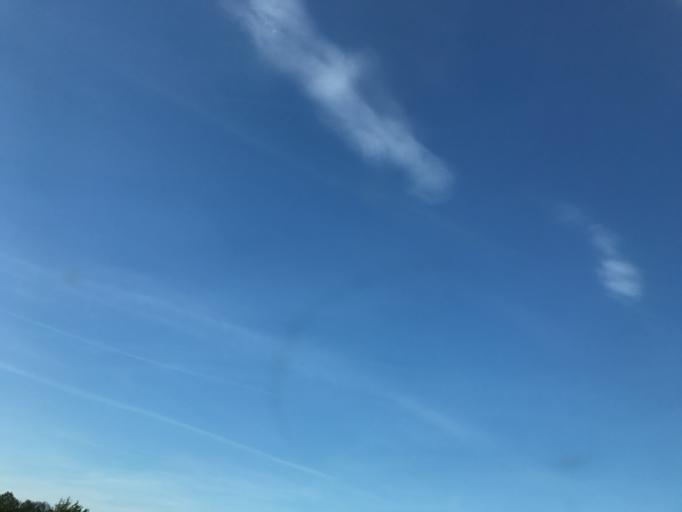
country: RS
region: Central Serbia
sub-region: Borski Okrug
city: Negotin
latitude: 44.1640
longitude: 22.3629
